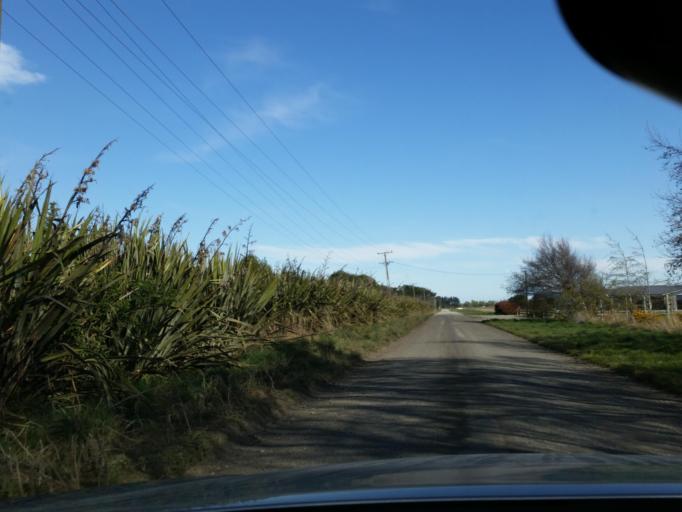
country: NZ
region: Southland
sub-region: Invercargill City
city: Invercargill
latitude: -46.3032
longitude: 168.3033
